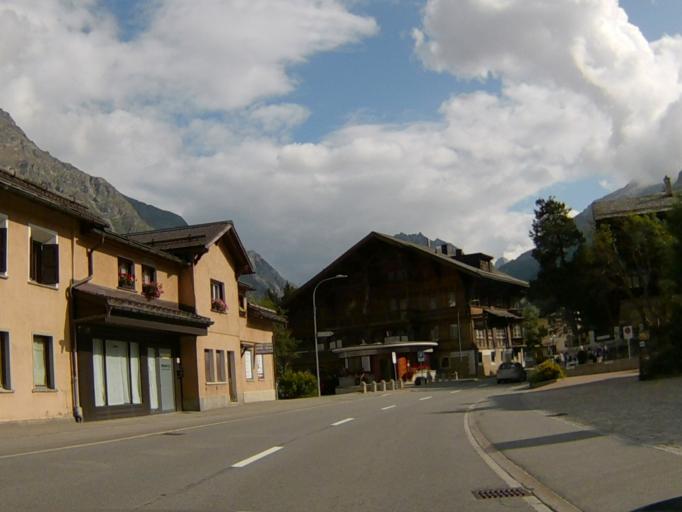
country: CH
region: Grisons
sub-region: Maloja District
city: Silvaplana
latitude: 46.4034
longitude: 9.6955
